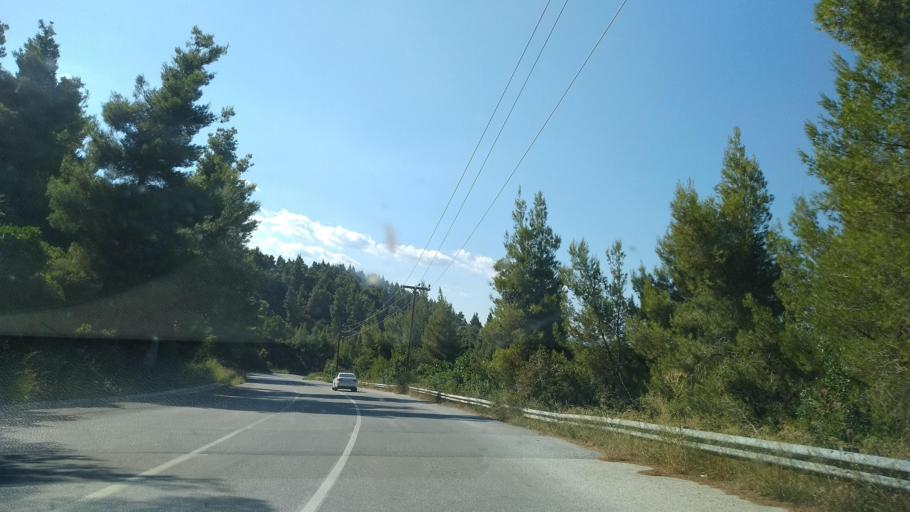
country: GR
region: Central Macedonia
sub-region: Nomos Chalkidikis
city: Agios Nikolaos
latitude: 40.2831
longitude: 23.6840
